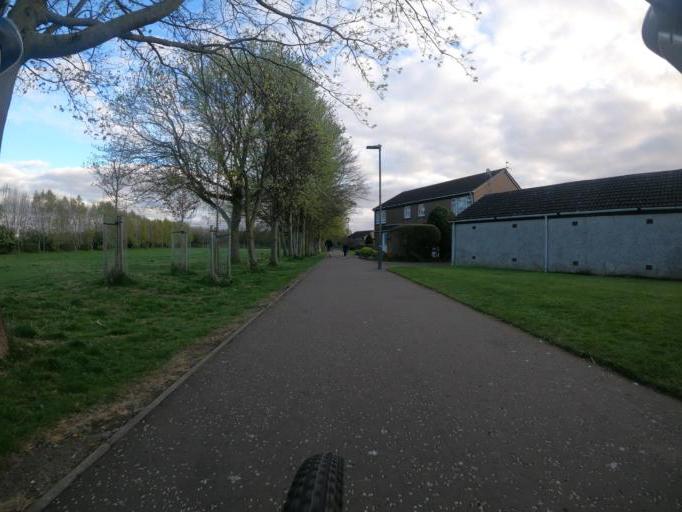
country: GB
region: Scotland
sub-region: Edinburgh
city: Currie
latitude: 55.9396
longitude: -3.3067
